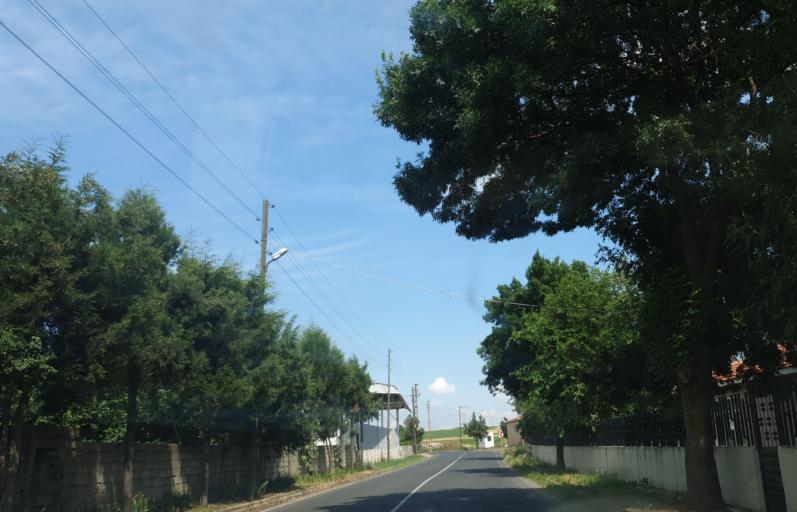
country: TR
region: Tekirdag
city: Muratli
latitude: 41.2208
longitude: 27.5464
